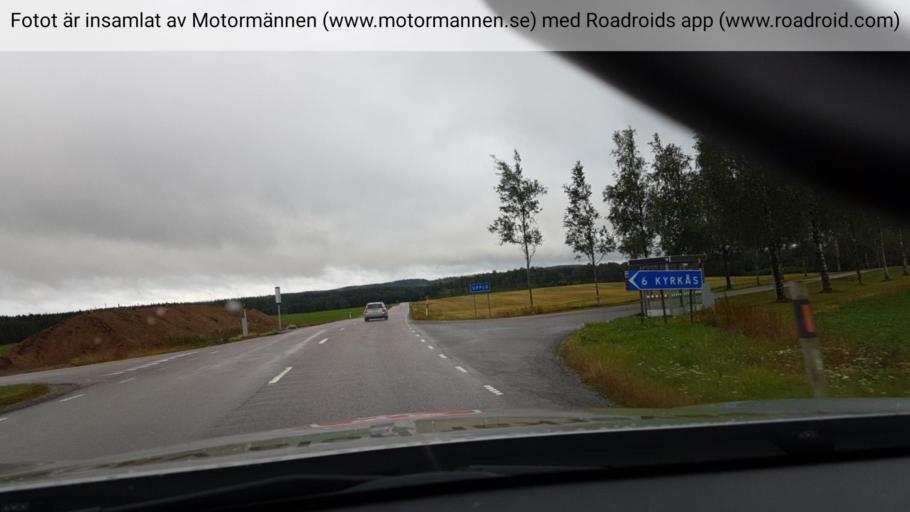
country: SE
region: Vaestra Goetaland
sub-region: Essunga Kommun
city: Nossebro
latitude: 58.1018
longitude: 12.6560
